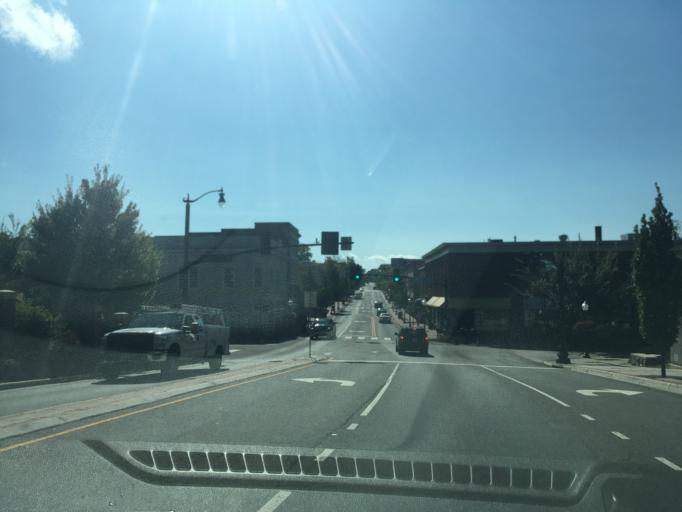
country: US
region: Virginia
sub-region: Montgomery County
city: Blacksburg
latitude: 37.2311
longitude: -80.4158
